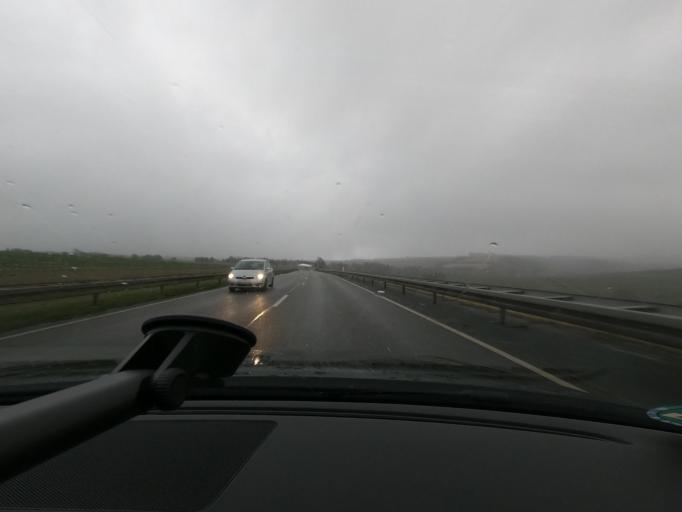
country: DE
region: Thuringia
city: Silberhausen
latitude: 51.3029
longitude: 10.3314
